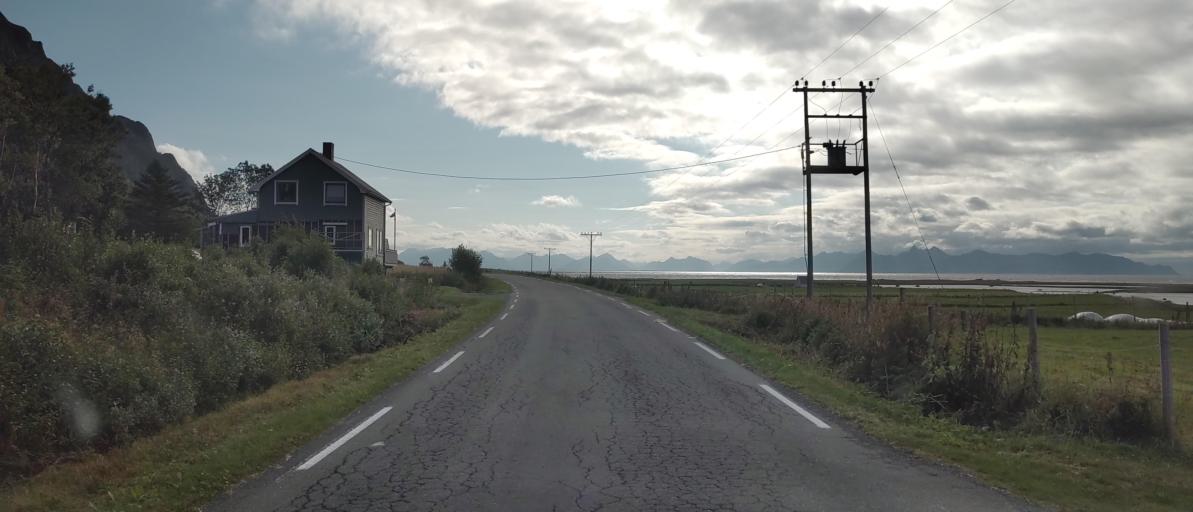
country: NO
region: Nordland
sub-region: Sortland
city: Sortland
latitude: 69.0694
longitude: 15.5436
